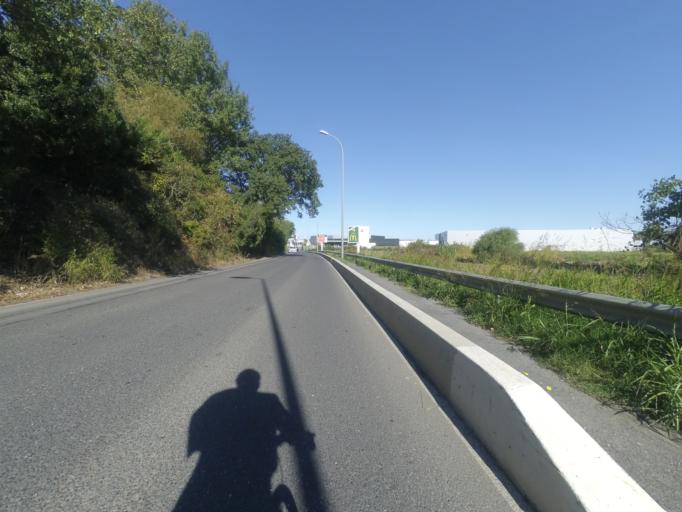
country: FR
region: Languedoc-Roussillon
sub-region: Departement des Pyrenees-Orientales
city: Perpignan
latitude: 42.6702
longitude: 2.8973
